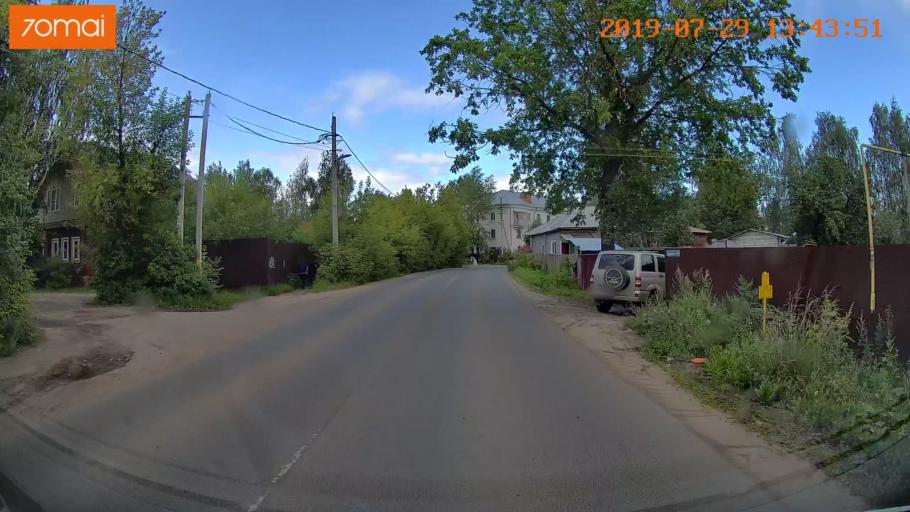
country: RU
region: Ivanovo
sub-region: Gorod Ivanovo
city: Ivanovo
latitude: 57.0071
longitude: 40.9298
